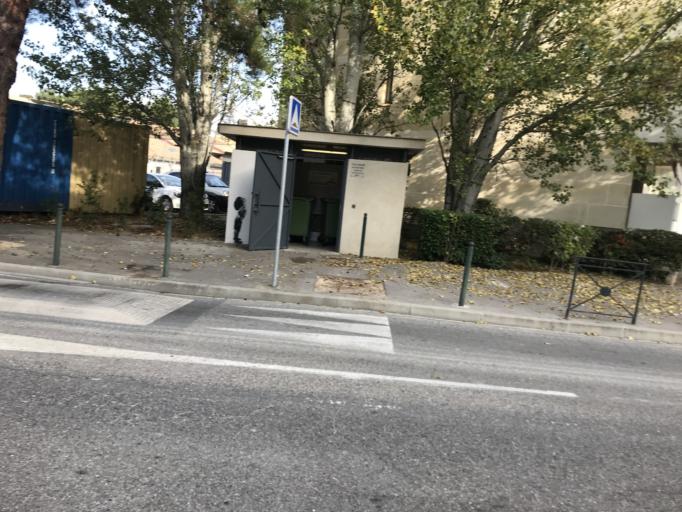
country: FR
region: Provence-Alpes-Cote d'Azur
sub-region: Departement des Bouches-du-Rhone
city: Aix-en-Provence
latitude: 43.5208
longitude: 5.4296
